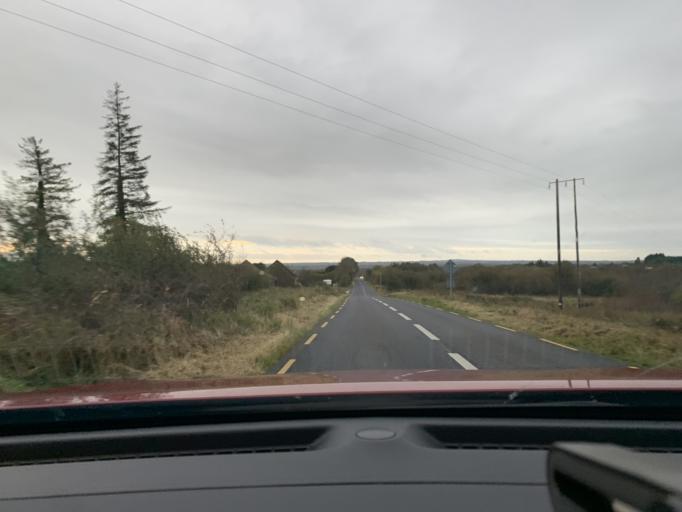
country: IE
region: Connaught
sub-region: Roscommon
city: Ballaghaderreen
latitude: 53.9411
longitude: -8.5440
